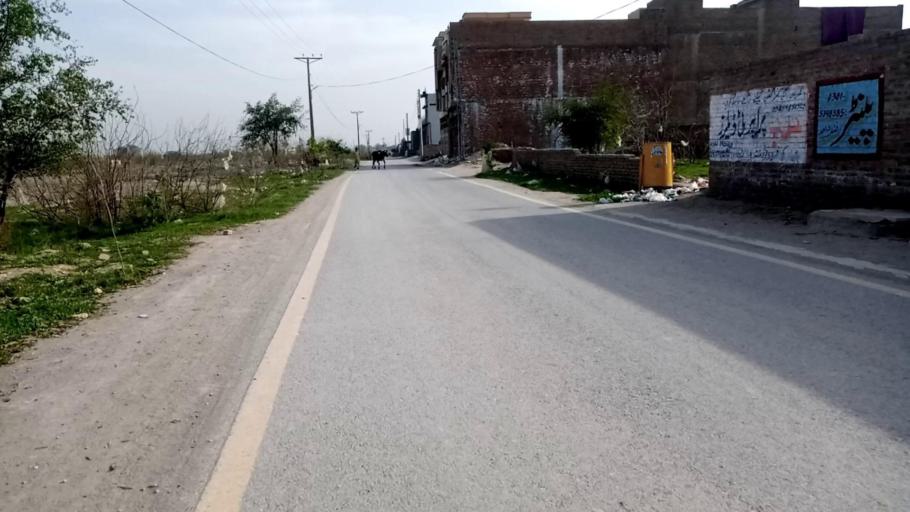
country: PK
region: Khyber Pakhtunkhwa
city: Peshawar
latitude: 34.0089
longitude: 71.4476
